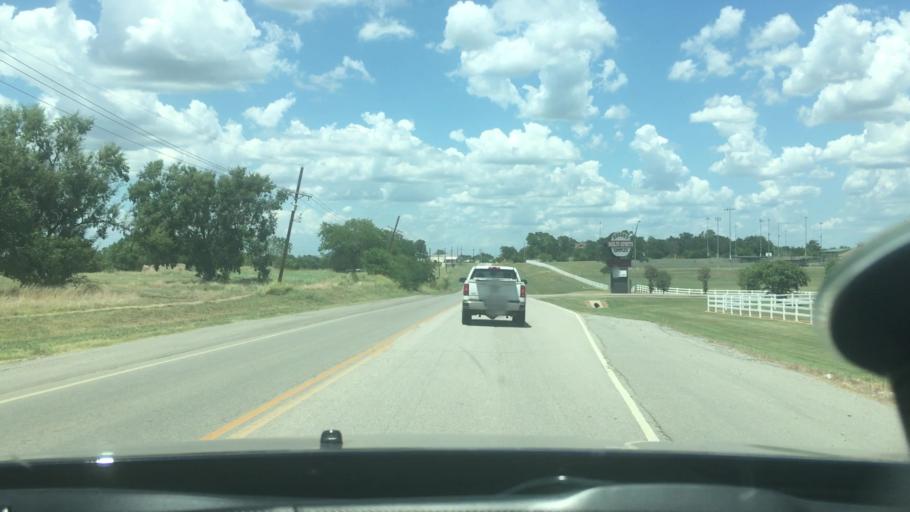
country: US
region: Oklahoma
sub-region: Bryan County
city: Durant
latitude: 33.9722
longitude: -96.3730
